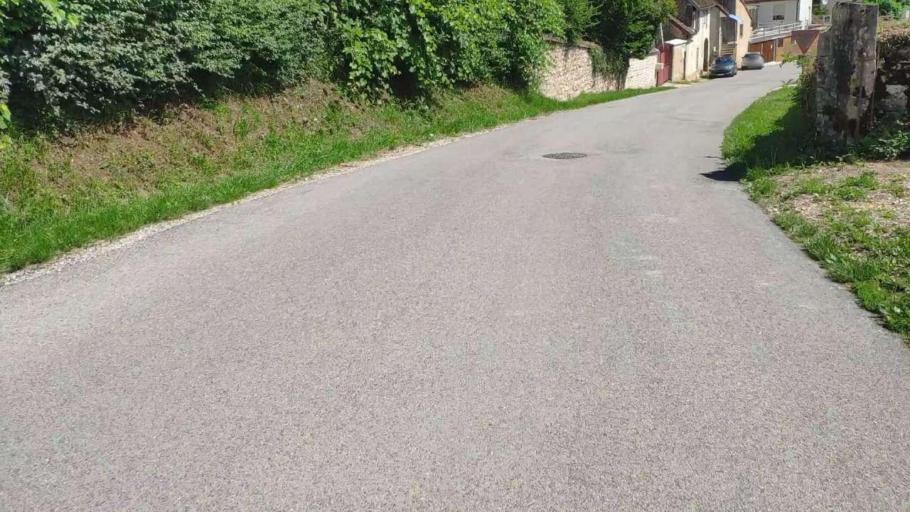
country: FR
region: Franche-Comte
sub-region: Departement du Jura
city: Bletterans
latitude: 46.8255
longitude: 5.5594
